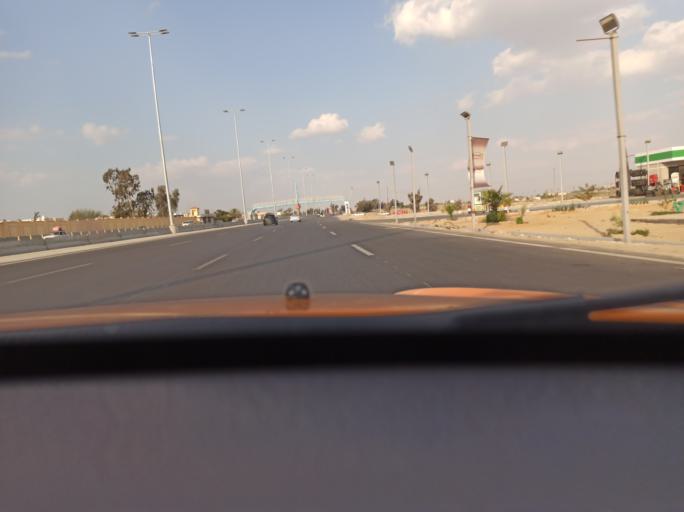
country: EG
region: Al Isma'iliyah
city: Ismailia
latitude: 30.6160
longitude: 32.2260
